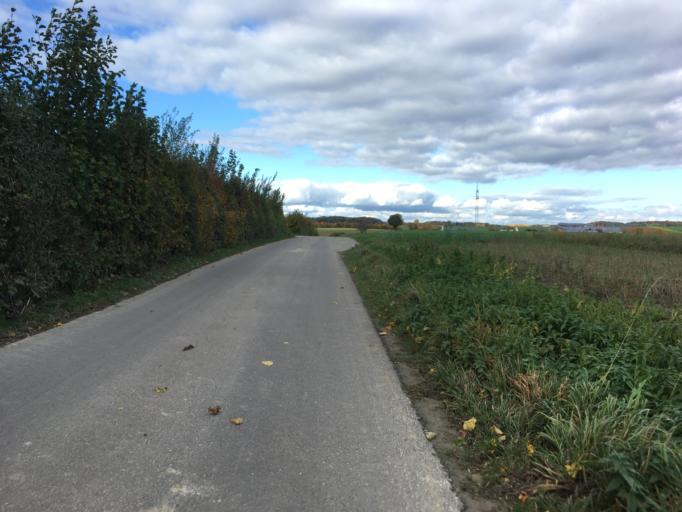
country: DE
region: Baden-Wuerttemberg
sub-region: Regierungsbezirk Stuttgart
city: Kupferzell
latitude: 49.2253
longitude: 9.7294
